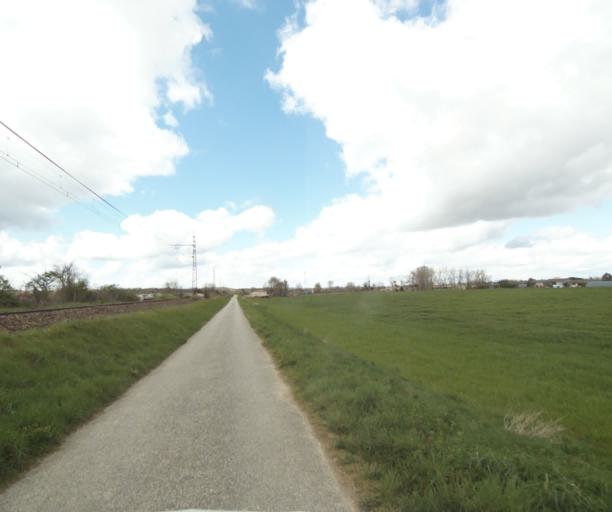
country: FR
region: Midi-Pyrenees
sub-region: Departement de l'Ariege
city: Saverdun
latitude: 43.2341
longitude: 1.5915
